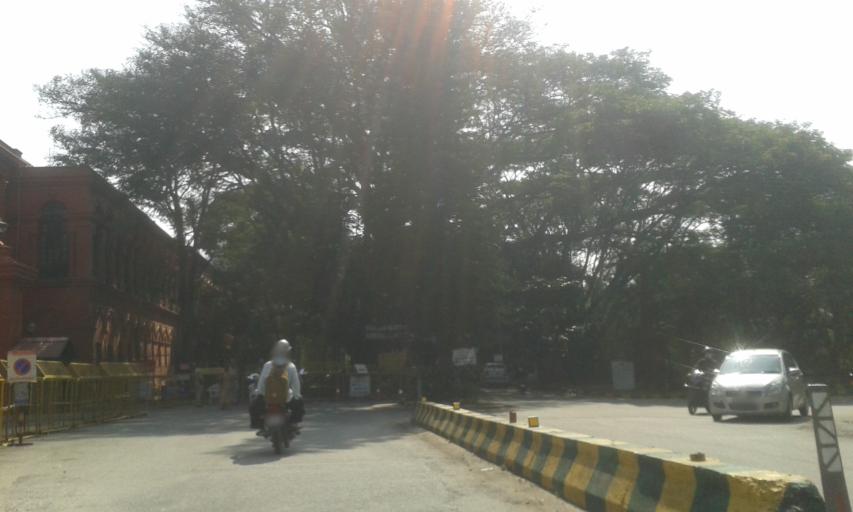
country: IN
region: Karnataka
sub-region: Bangalore Urban
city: Bangalore
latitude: 12.9774
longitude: 77.5912
